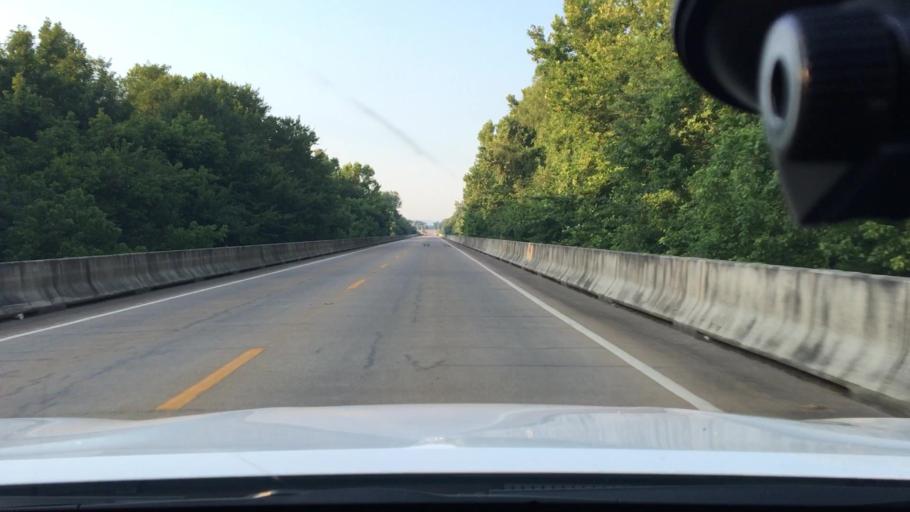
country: US
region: Arkansas
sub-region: Johnson County
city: Clarksville
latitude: 35.4021
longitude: -93.5312
